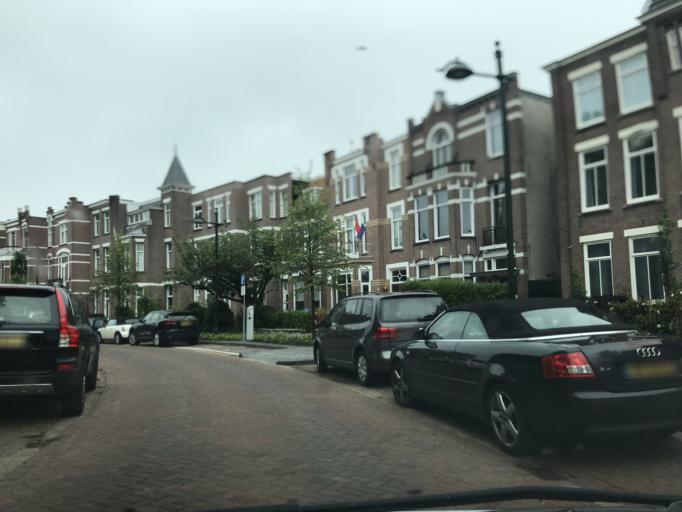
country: NL
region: North Brabant
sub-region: Gemeente Breda
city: Breda
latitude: 51.5730
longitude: 4.7777
